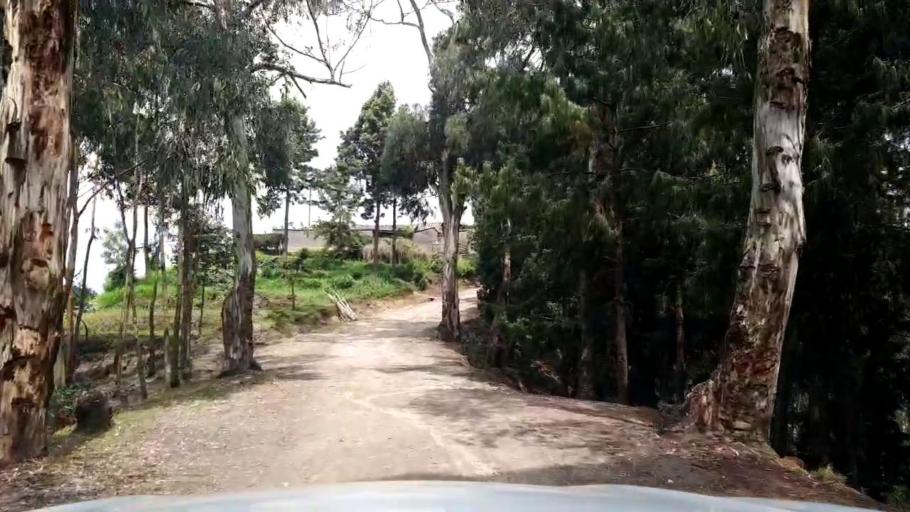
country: RW
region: Western Province
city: Kibuye
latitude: -1.9376
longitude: 29.4615
